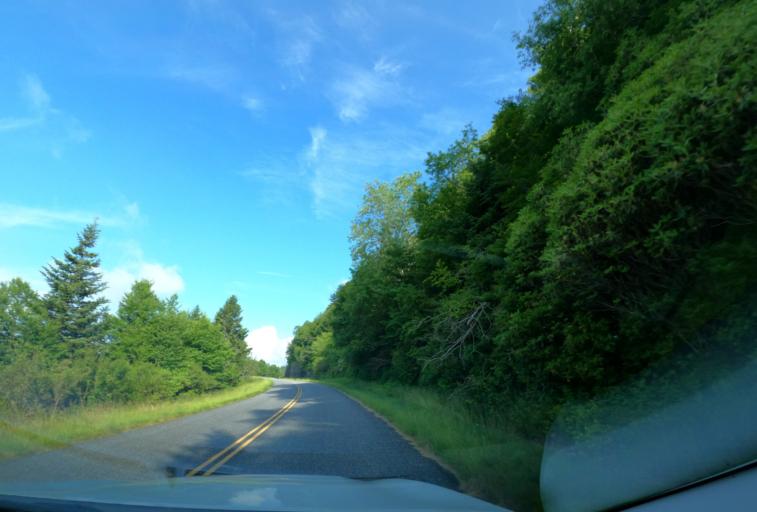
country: US
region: North Carolina
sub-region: Haywood County
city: Hazelwood
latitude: 35.3001
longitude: -82.9280
